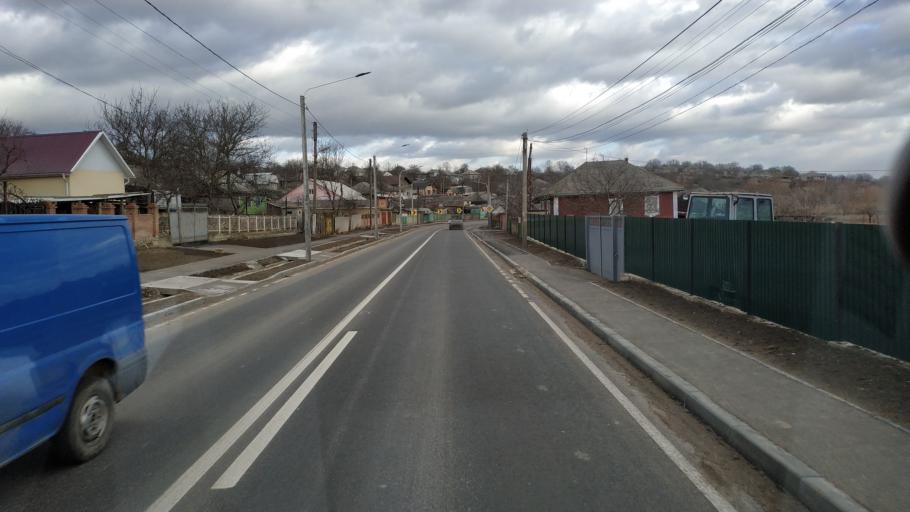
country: MD
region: Calarasi
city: Calarasi
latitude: 47.2896
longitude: 28.1911
